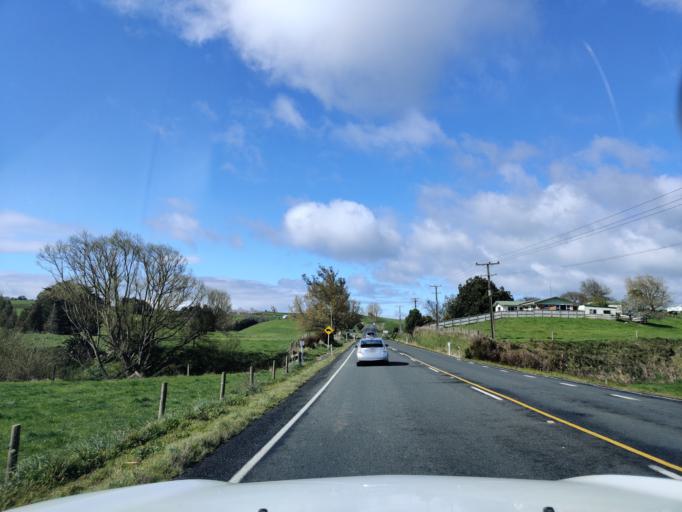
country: NZ
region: Waikato
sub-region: Otorohanga District
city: Otorohanga
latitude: -38.0882
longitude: 175.1819
